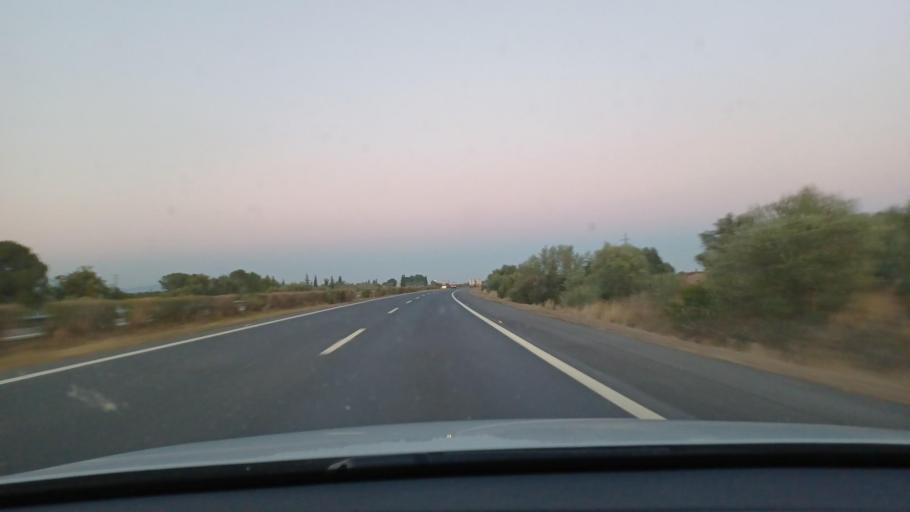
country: ES
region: Catalonia
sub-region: Provincia de Tarragona
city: Masdenverge
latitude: 40.6928
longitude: 0.5311
